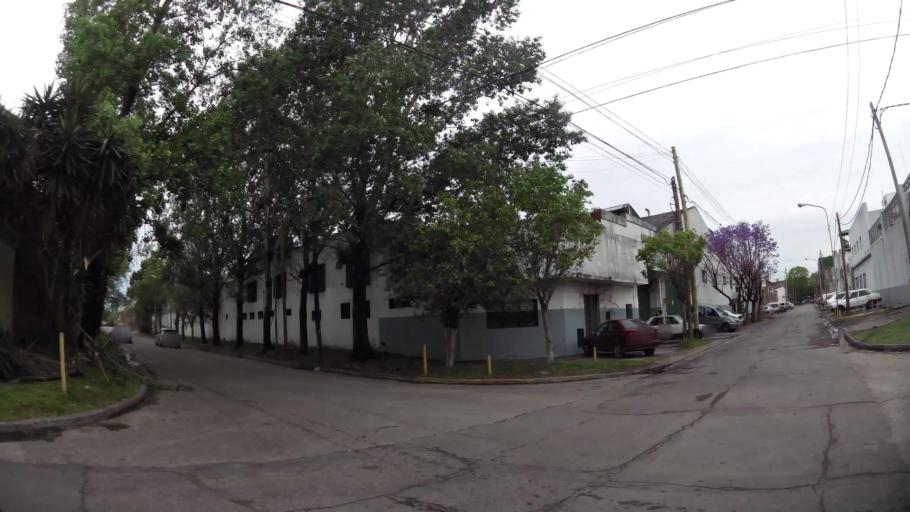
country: AR
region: Buenos Aires
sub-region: Partido de Lanus
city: Lanus
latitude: -34.7125
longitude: -58.3610
